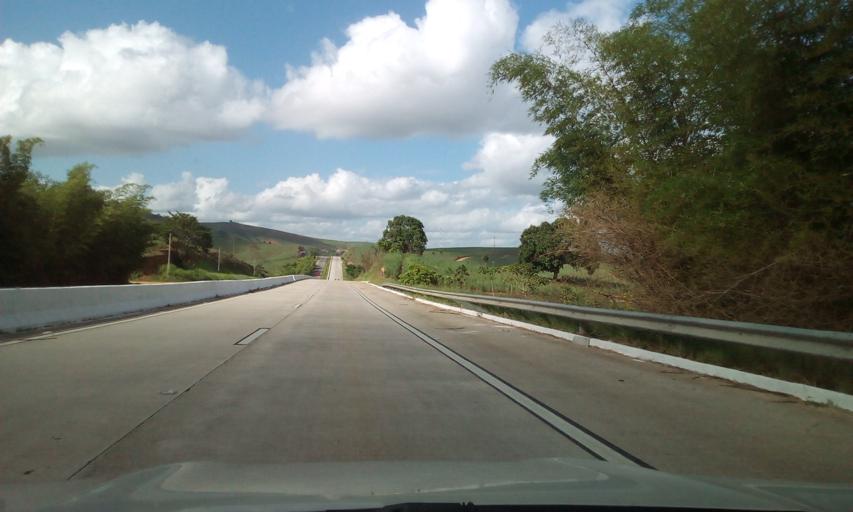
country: BR
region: Alagoas
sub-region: Novo Lino
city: Novo Lino
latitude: -8.9672
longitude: -35.6724
